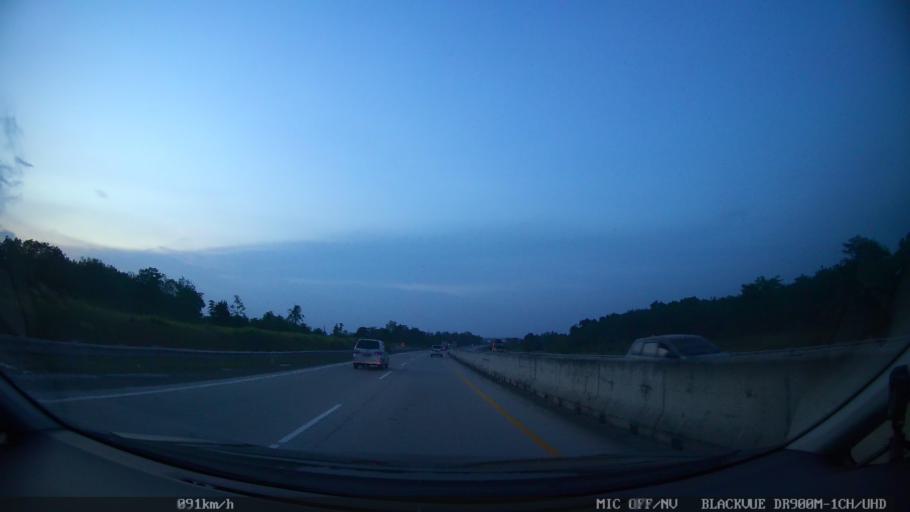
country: ID
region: Lampung
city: Sidorejo
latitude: -5.6400
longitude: 105.5714
